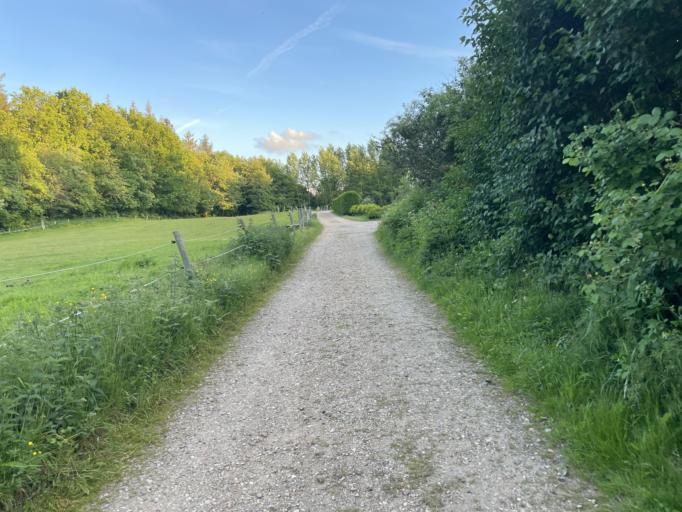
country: DE
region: Schleswig-Holstein
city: Husum
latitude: 54.4726
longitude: 9.0718
